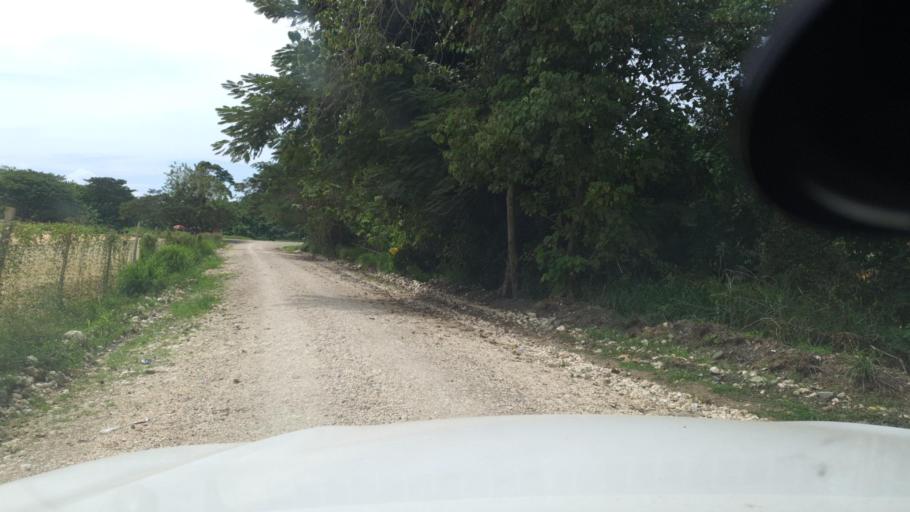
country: SB
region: Guadalcanal
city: Honiara
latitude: -9.4139
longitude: 159.8932
